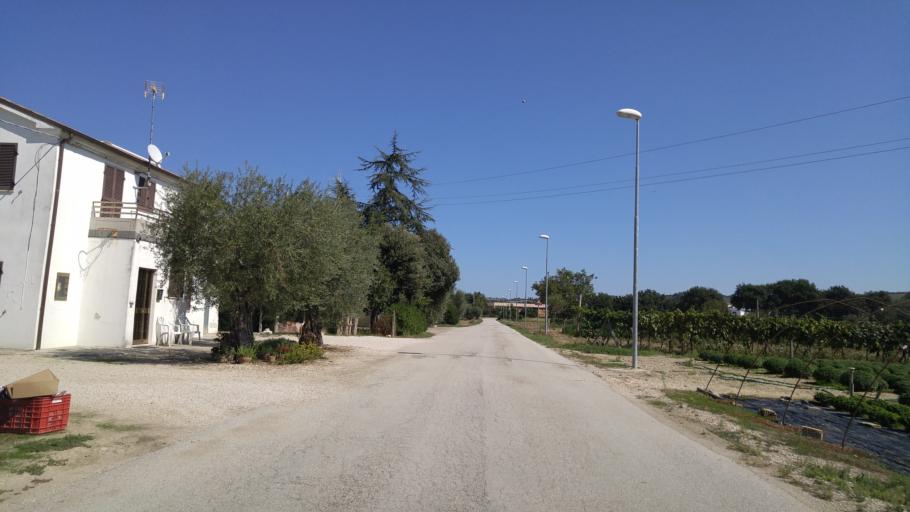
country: IT
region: The Marches
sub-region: Provincia di Pesaro e Urbino
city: Villanova
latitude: 43.7530
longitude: 12.9420
